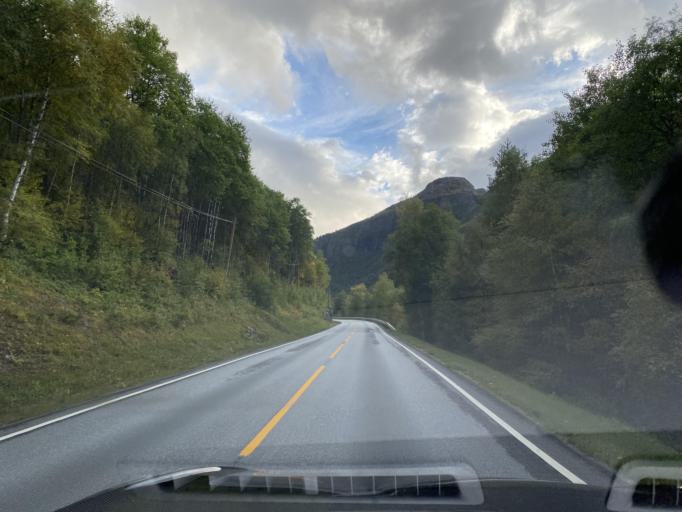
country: NO
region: Oppland
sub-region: Lom
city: Fossbergom
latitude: 61.8060
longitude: 8.4563
